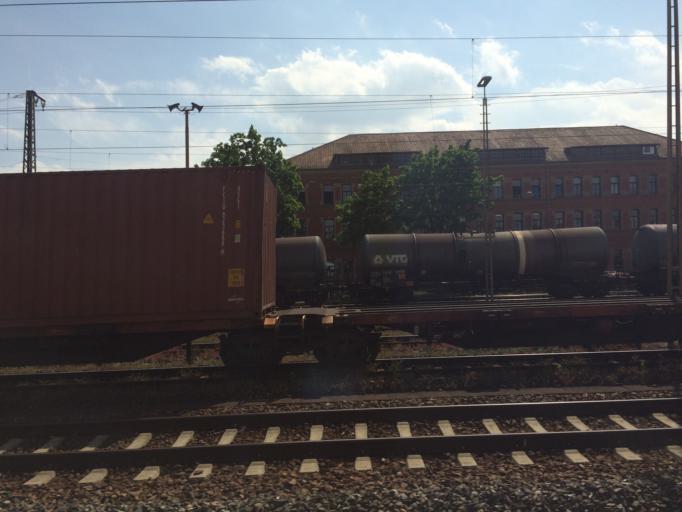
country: DE
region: Bavaria
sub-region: Regierungsbezirk Mittelfranken
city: Furth
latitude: 49.4667
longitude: 11.0035
